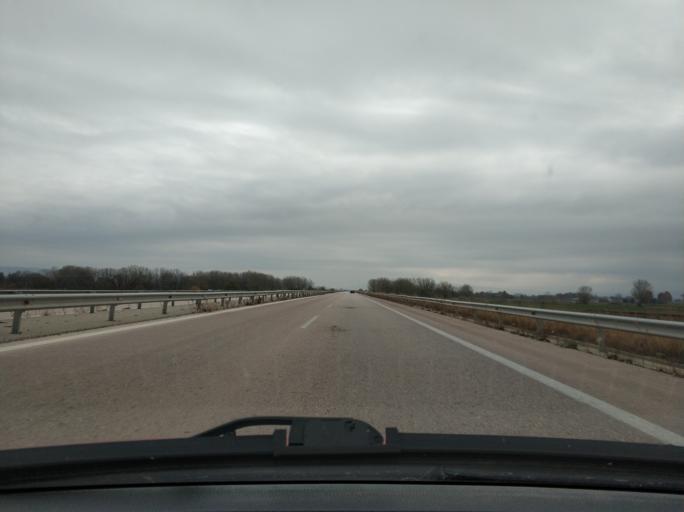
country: GR
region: Central Macedonia
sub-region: Nomos Thessalonikis
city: Kavallari
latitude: 40.7310
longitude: 23.0549
